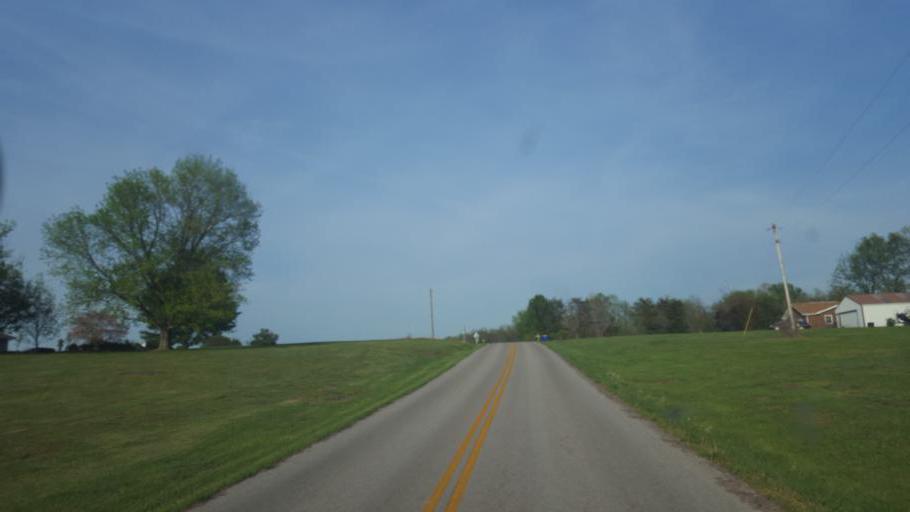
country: US
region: Kentucky
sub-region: Allen County
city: Scottsville
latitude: 36.9069
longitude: -86.1193
